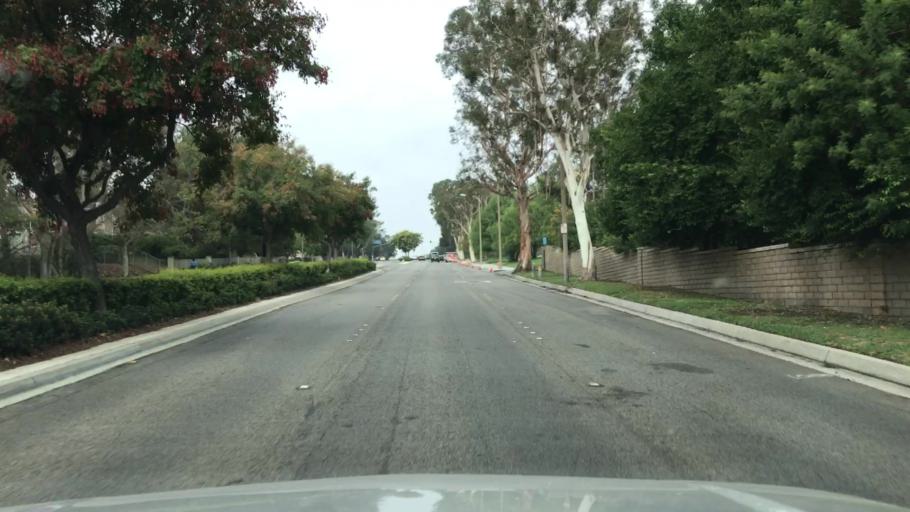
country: US
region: California
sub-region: Los Angeles County
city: Santa Clarita
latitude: 34.3948
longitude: -118.5616
